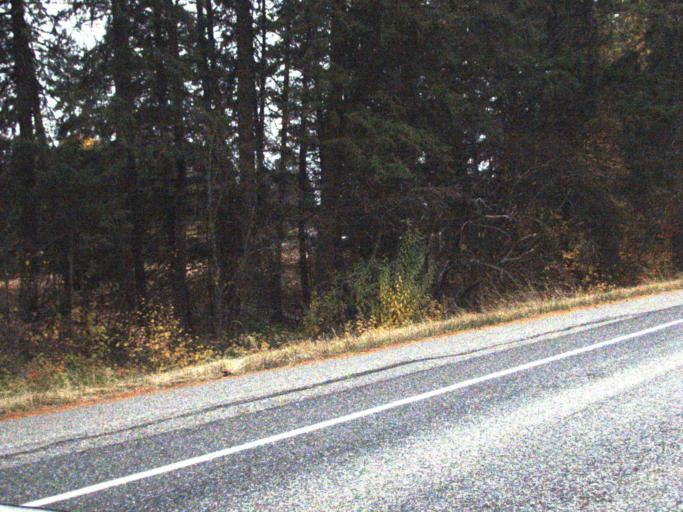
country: US
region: Washington
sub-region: Stevens County
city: Kettle Falls
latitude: 48.6717
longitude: -118.1172
